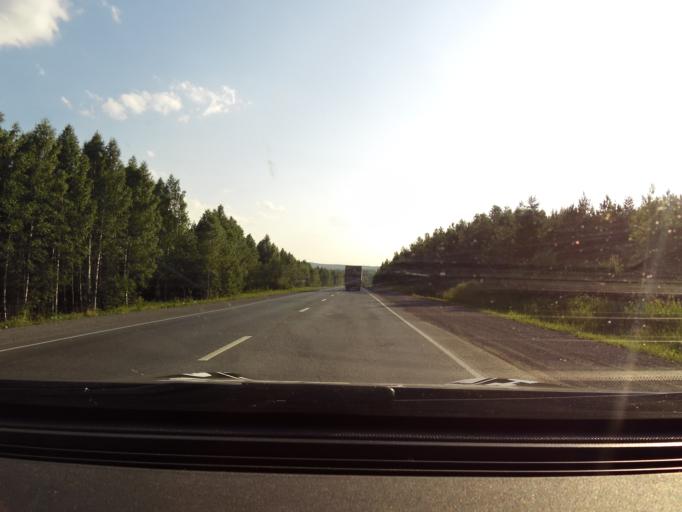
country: RU
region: Sverdlovsk
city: Druzhinino
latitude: 56.8413
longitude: 59.6670
